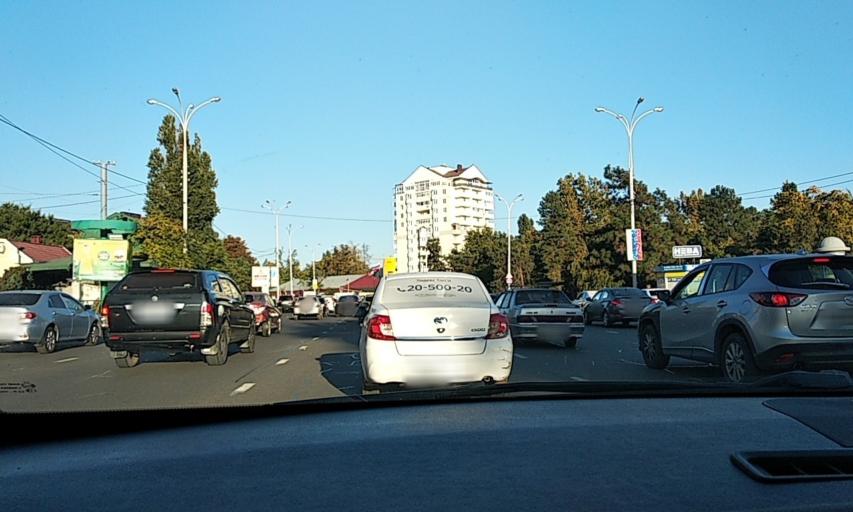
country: RU
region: Krasnodarskiy
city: Krasnodar
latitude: 45.0242
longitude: 38.9947
